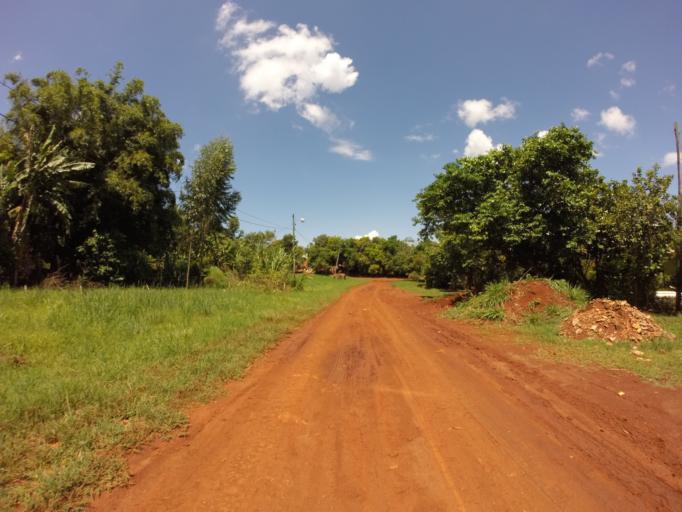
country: PY
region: Alto Parana
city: Ciudad del Este
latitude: -25.3990
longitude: -54.6368
